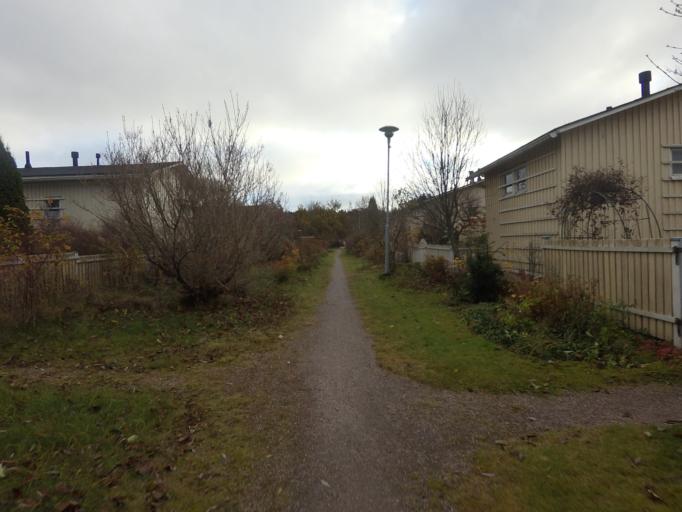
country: FI
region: Uusimaa
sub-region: Helsinki
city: Kauniainen
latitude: 60.1798
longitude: 24.7027
